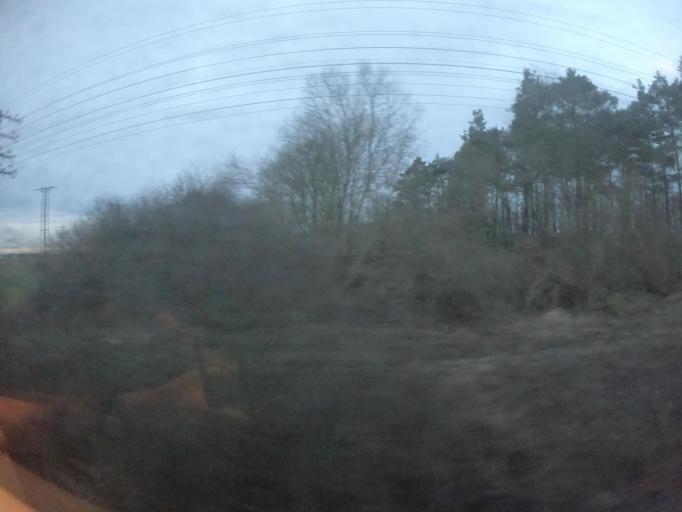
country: PL
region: West Pomeranian Voivodeship
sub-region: Powiat drawski
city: Zlocieniec
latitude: 53.5275
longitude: 16.0438
